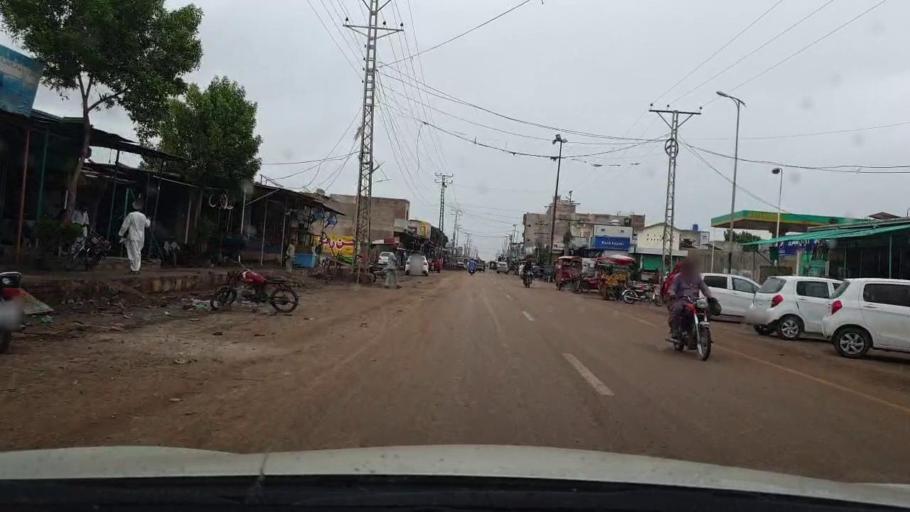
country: PK
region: Sindh
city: Kario
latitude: 24.6533
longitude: 68.5324
